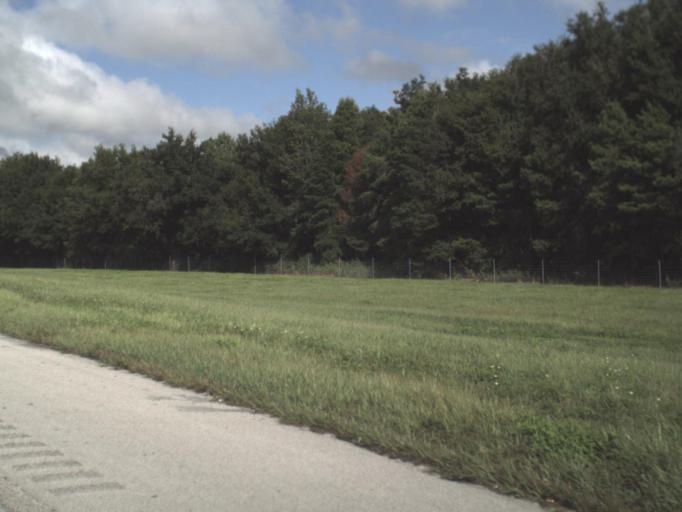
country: US
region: Florida
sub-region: Polk County
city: Polk City
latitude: 28.1578
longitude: -81.8224
